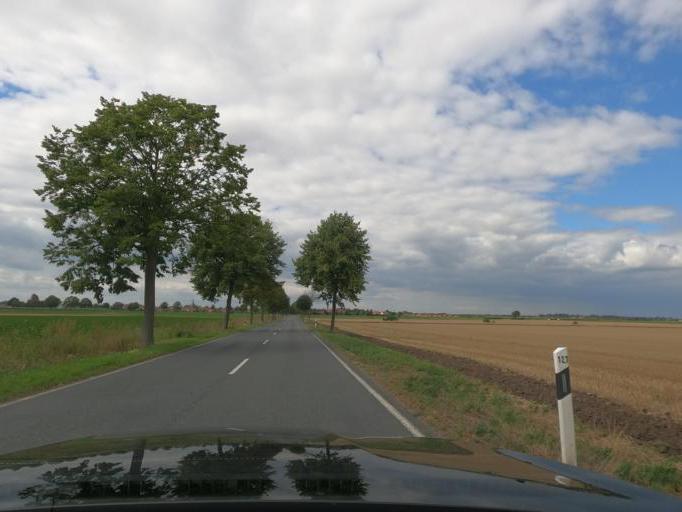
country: DE
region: Lower Saxony
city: Algermissen
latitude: 52.2483
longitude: 9.9922
